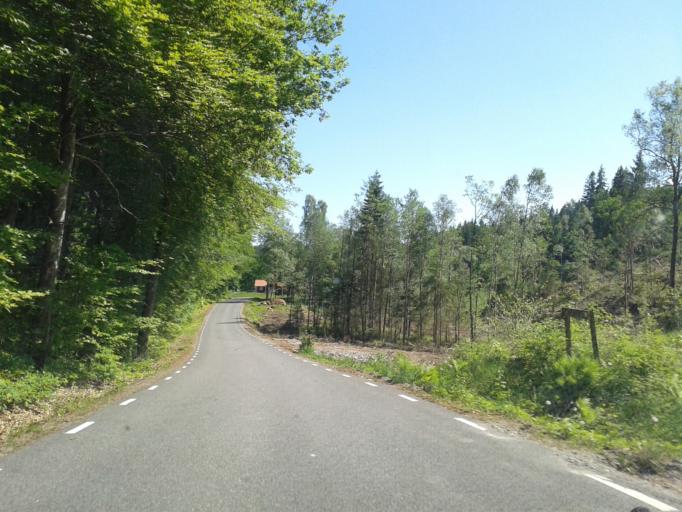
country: SE
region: Vaestra Goetaland
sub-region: Kungalvs Kommun
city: Diserod
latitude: 57.9627
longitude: 12.0067
